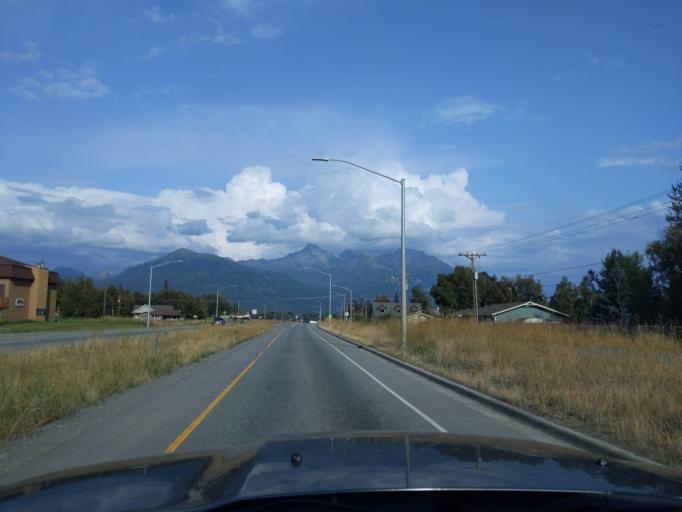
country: US
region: Alaska
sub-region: Matanuska-Susitna Borough
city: Palmer
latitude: 61.6067
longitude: -149.1296
